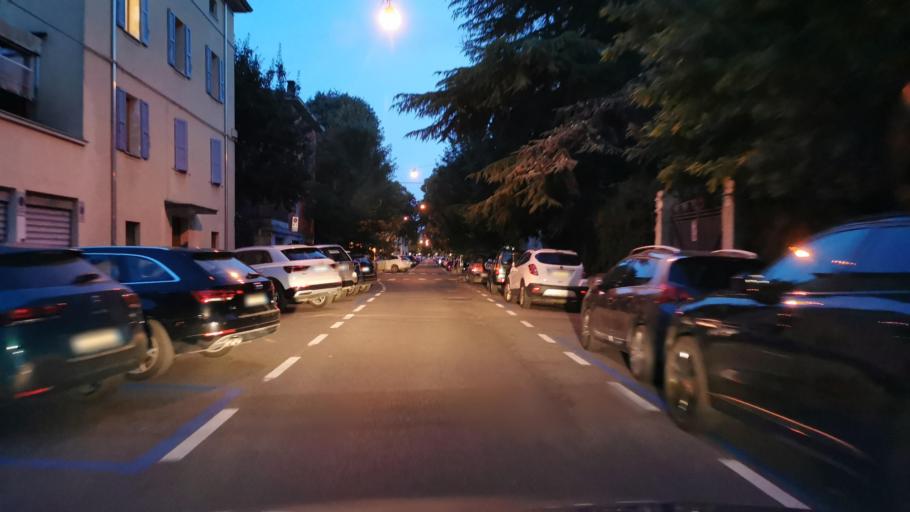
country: IT
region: Emilia-Romagna
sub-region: Provincia di Modena
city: Modena
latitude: 44.6419
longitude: 10.9319
